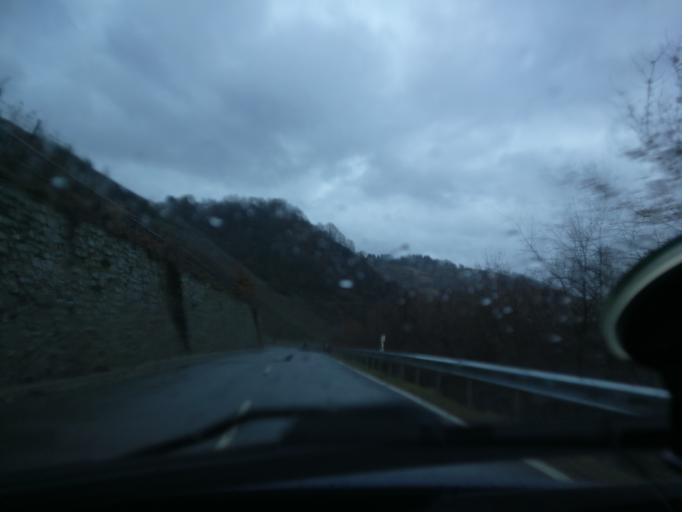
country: DE
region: Rheinland-Pfalz
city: Minheim
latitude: 49.8577
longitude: 6.9165
